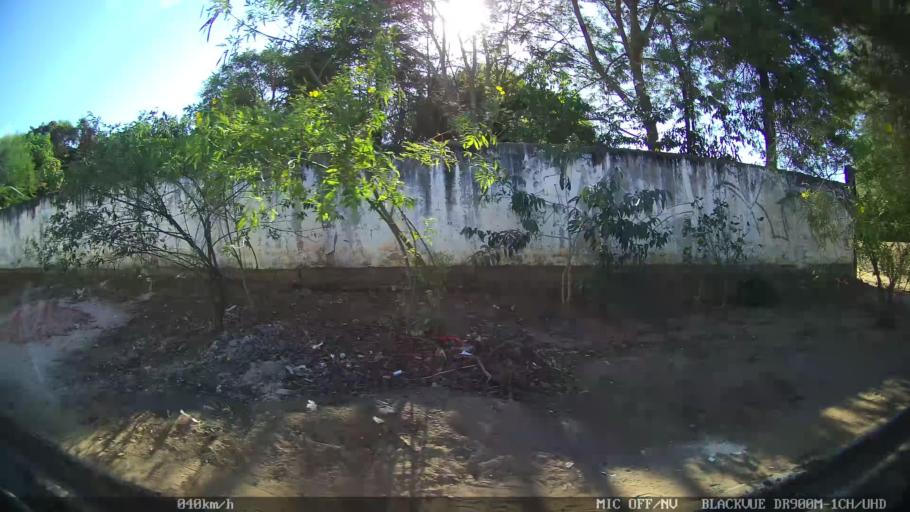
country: BR
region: Sao Paulo
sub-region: Franca
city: Franca
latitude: -20.4789
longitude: -47.4184
